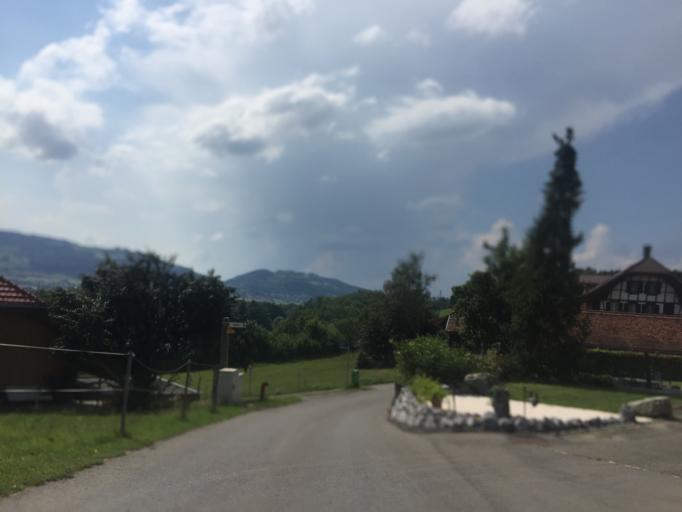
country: CH
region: Bern
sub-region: Bern-Mittelland District
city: Rubigen
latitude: 46.9028
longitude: 7.5317
